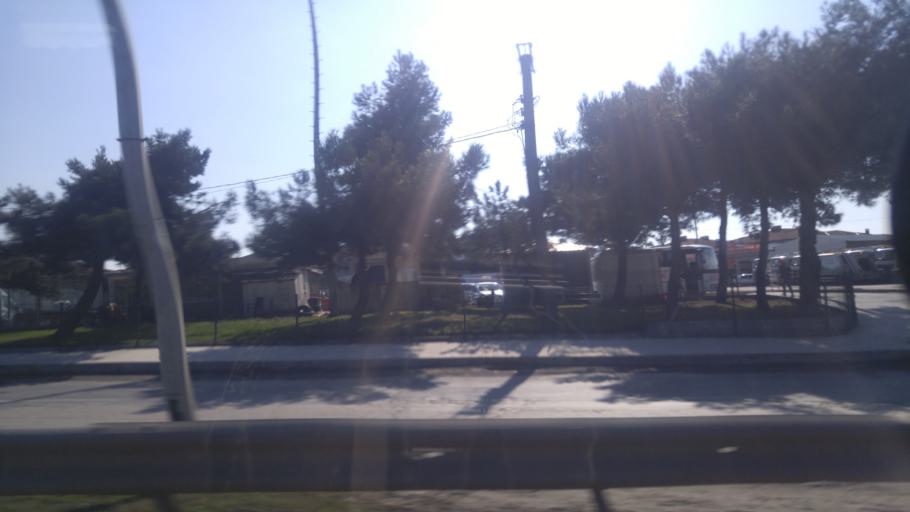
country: TR
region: Istanbul
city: Silivri
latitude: 41.0733
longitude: 28.2642
